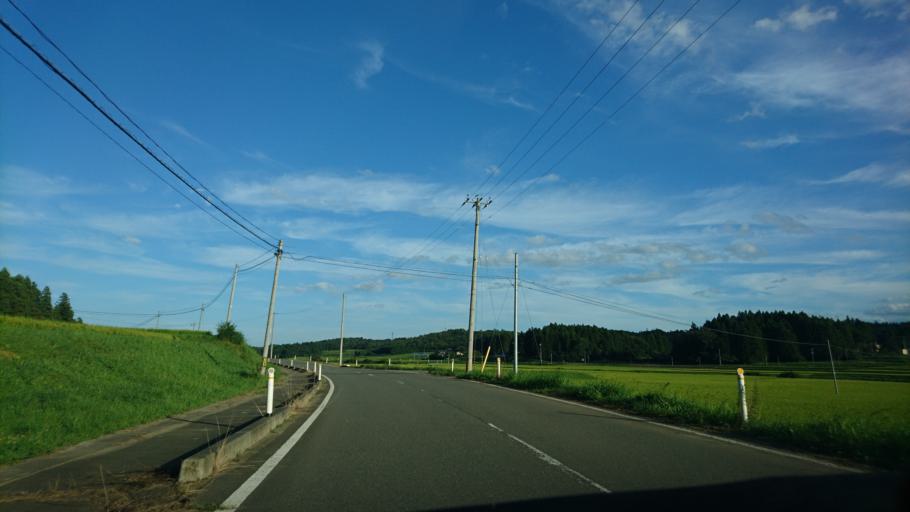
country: JP
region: Iwate
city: Ichinoseki
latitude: 38.8477
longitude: 141.1131
